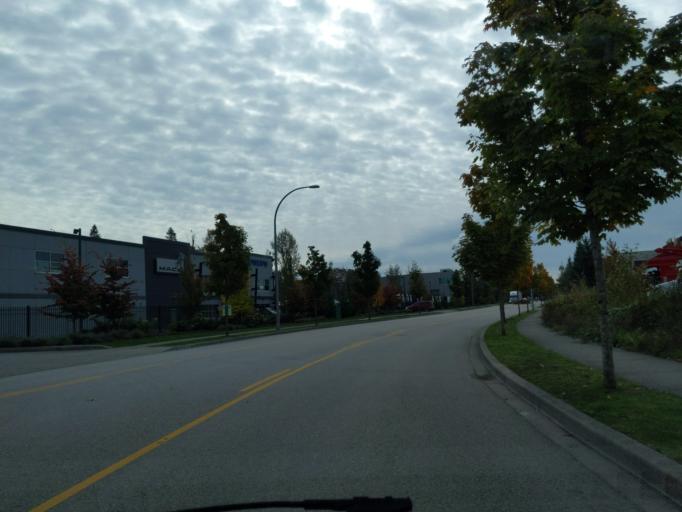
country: CA
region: British Columbia
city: Walnut Grove
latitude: 49.1809
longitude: -122.6603
